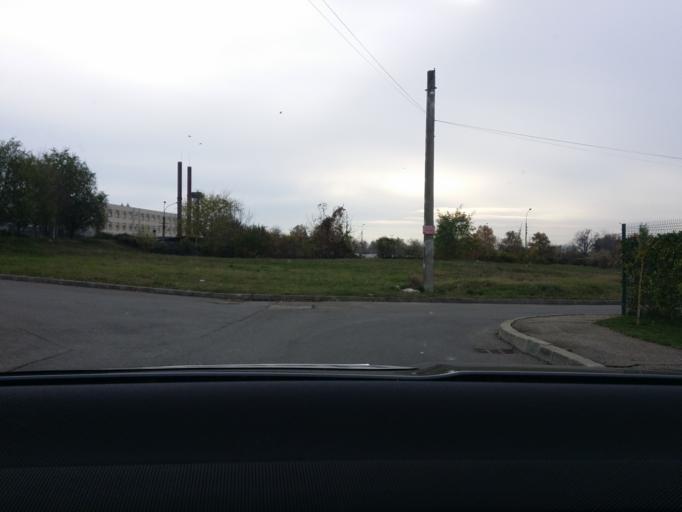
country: RO
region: Prahova
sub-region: Municipiul Campina
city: Campina
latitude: 45.1150
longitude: 25.7402
